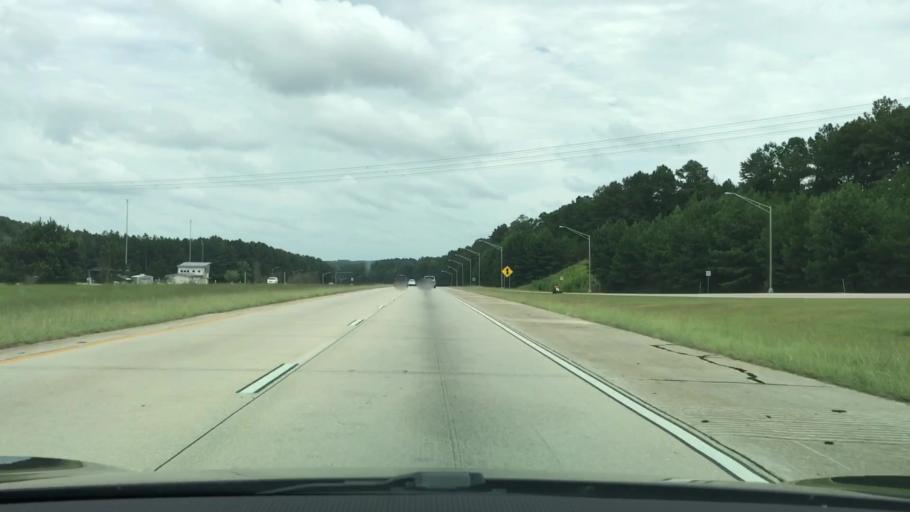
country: US
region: Georgia
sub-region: Troup County
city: Hogansville
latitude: 33.0851
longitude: -84.9160
